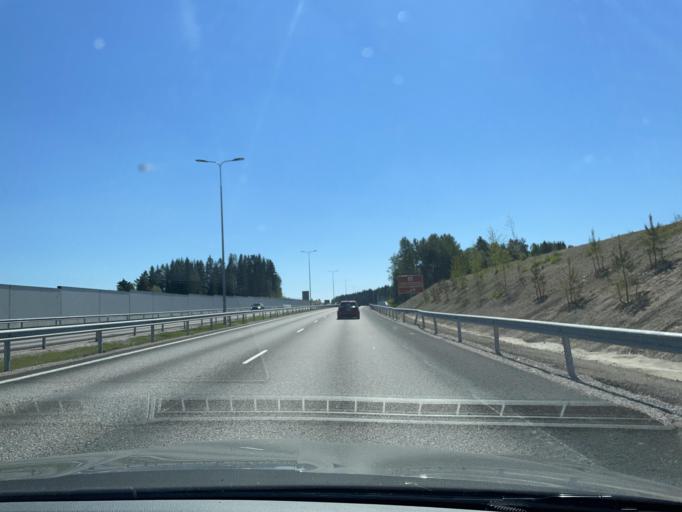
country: FI
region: Central Finland
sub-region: Jyvaeskylae
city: Jyvaeskylae
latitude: 62.4215
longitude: 25.6935
